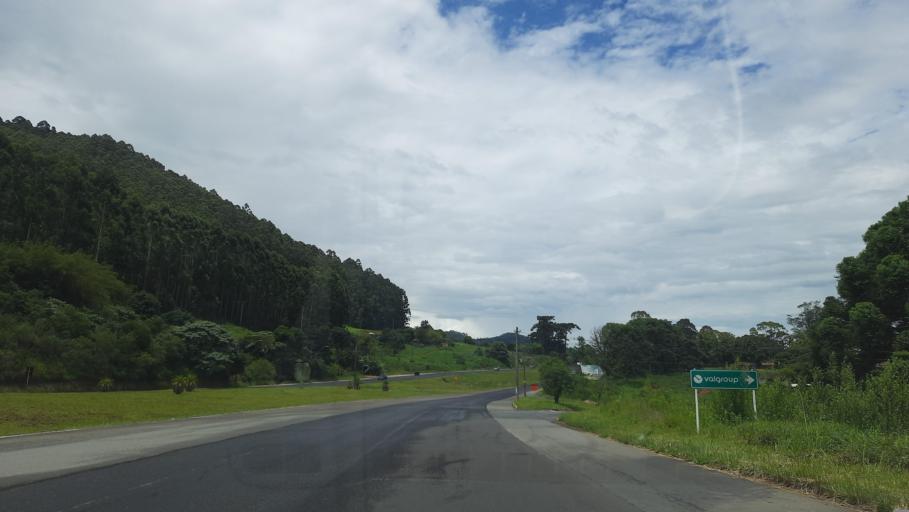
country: BR
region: Minas Gerais
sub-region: Pocos De Caldas
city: Pocos de Caldas
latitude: -21.7994
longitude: -46.6485
